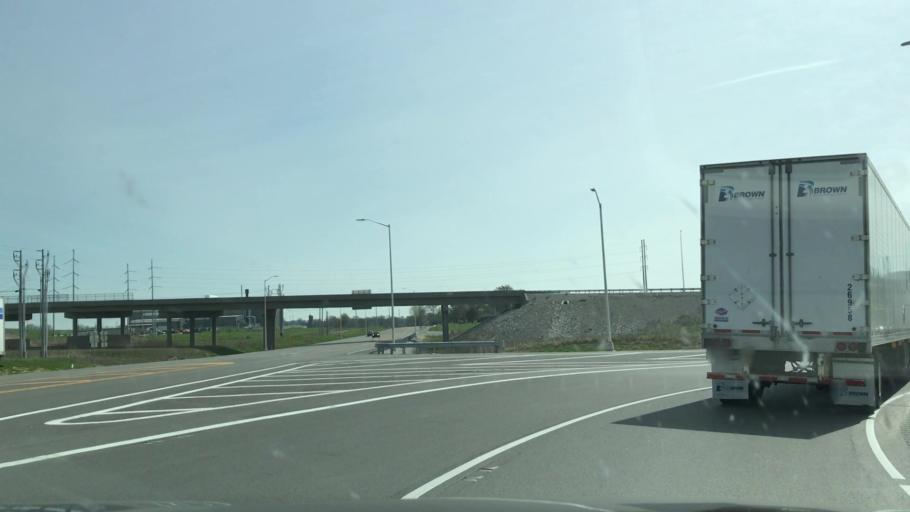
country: US
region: Kentucky
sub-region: Warren County
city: Bowling Green
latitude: 37.0329
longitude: -86.3140
